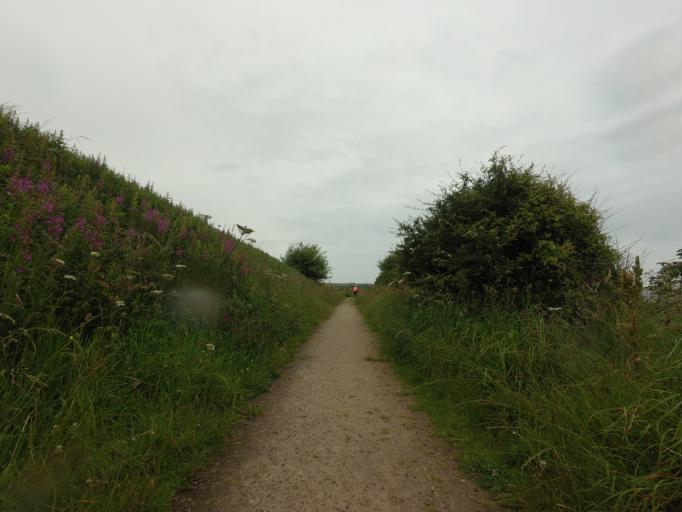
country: GB
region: Scotland
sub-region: Moray
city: Cullen
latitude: 57.6911
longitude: -2.8275
